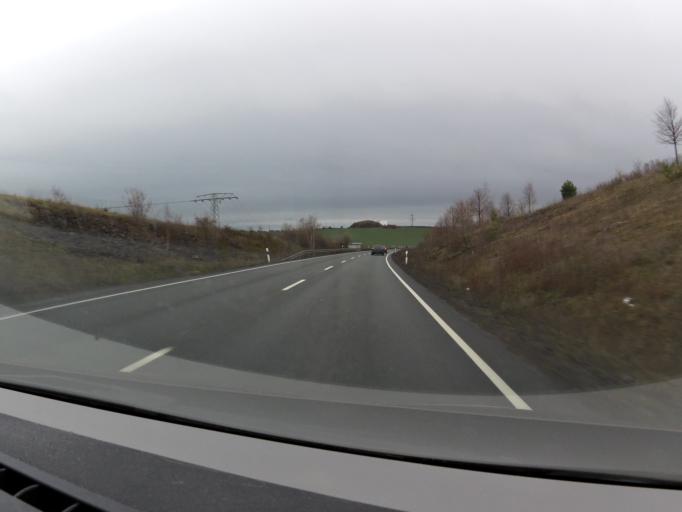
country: DE
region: Saxony-Anhalt
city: Grossorner
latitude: 51.6290
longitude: 11.4790
